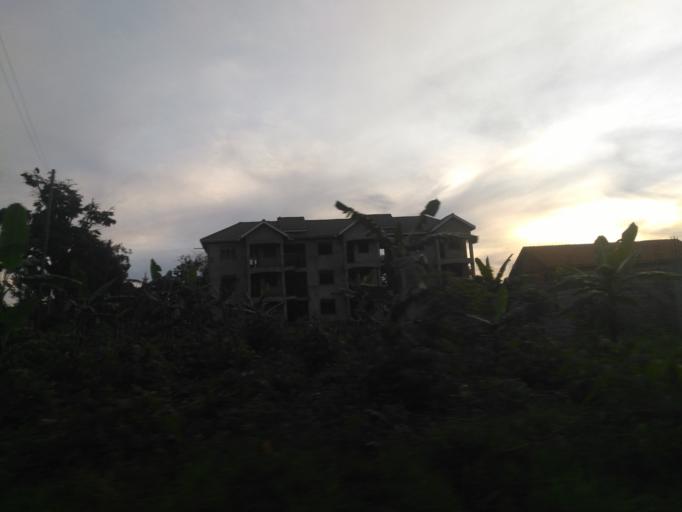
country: UG
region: Eastern Region
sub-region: Jinja District
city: Jinja
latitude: 0.4285
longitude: 33.2033
